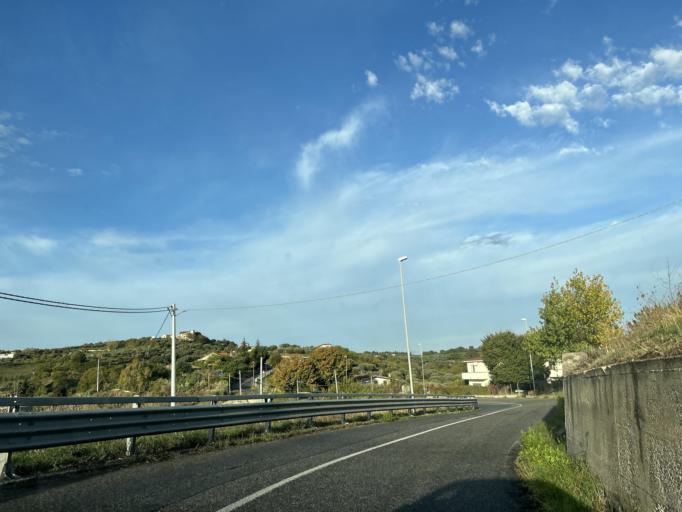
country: IT
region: Calabria
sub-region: Provincia di Catanzaro
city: Staletti
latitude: 38.7662
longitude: 16.5305
